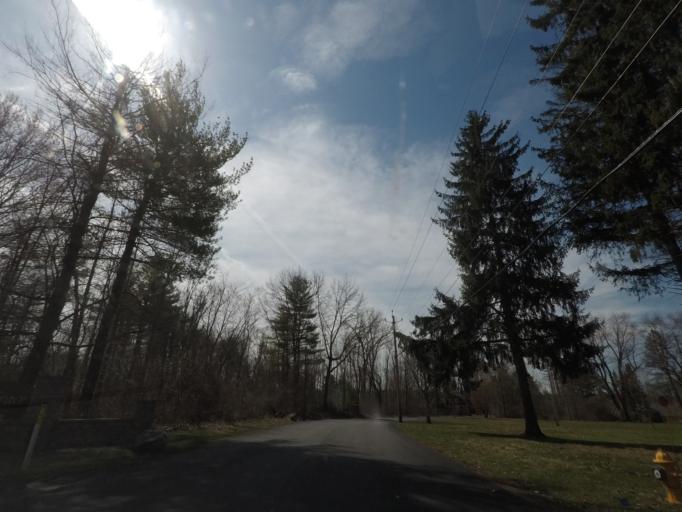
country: US
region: New York
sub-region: Saratoga County
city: Mechanicville
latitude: 42.8672
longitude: -73.7248
